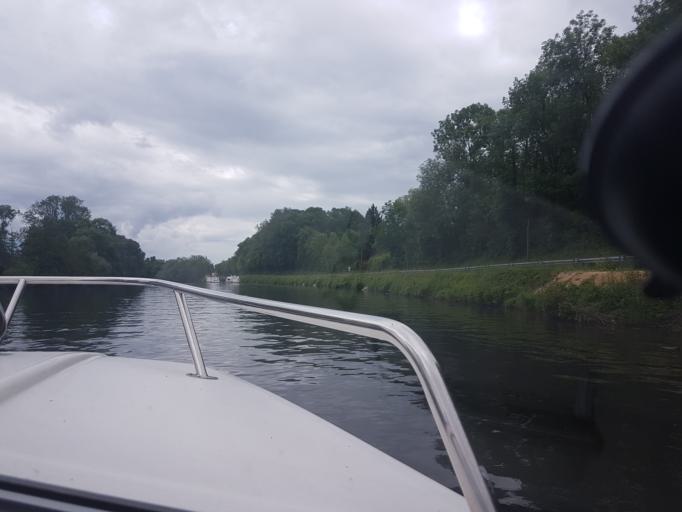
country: FR
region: Bourgogne
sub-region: Departement de l'Yonne
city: Champs-sur-Yonne
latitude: 47.7432
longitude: 3.5878
